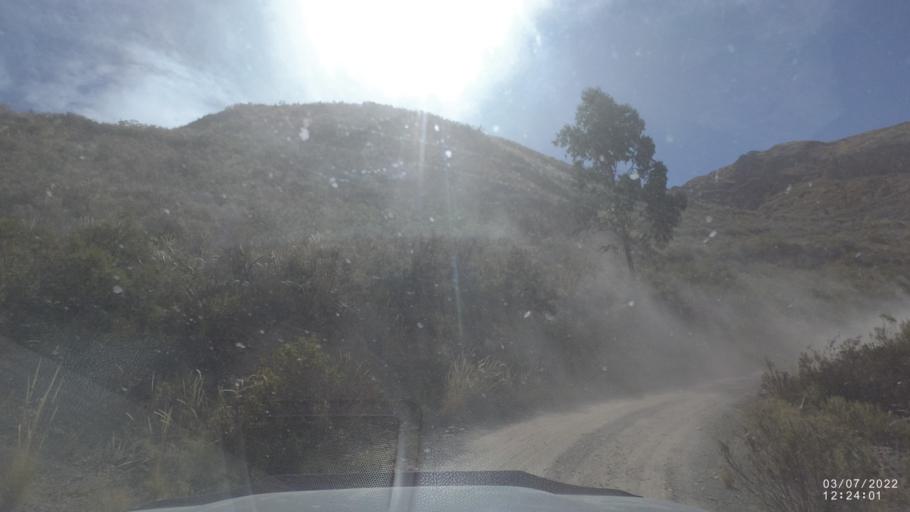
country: BO
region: Cochabamba
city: Irpa Irpa
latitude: -17.8142
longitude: -66.6190
